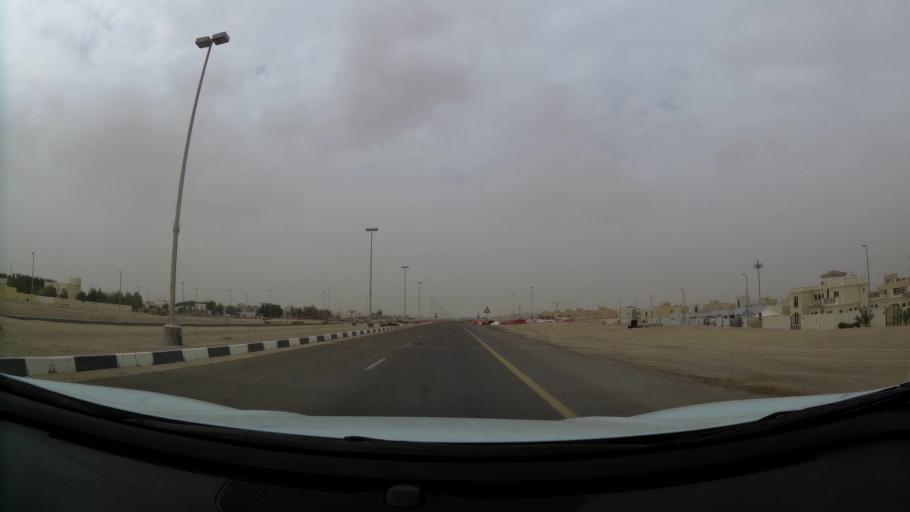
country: AE
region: Abu Dhabi
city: Abu Dhabi
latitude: 24.4300
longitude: 54.7437
